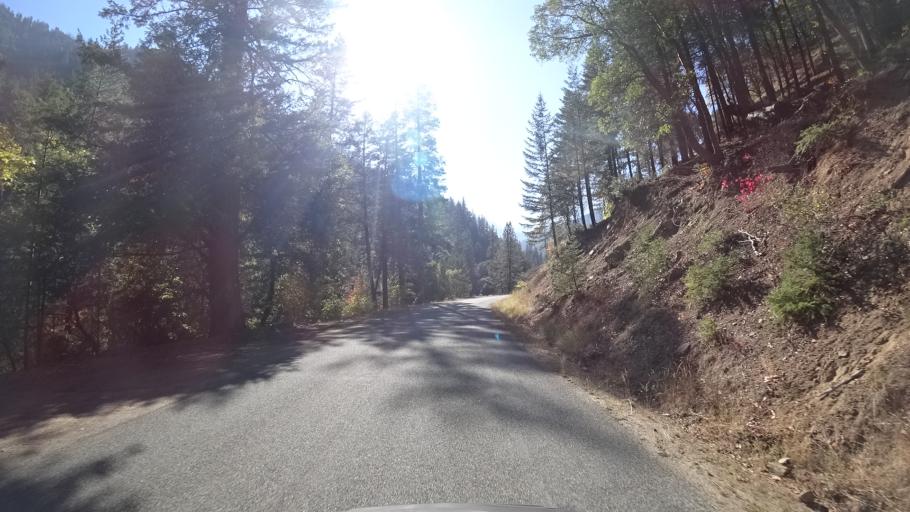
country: US
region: California
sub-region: Siskiyou County
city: Happy Camp
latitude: 41.6584
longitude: -123.1126
